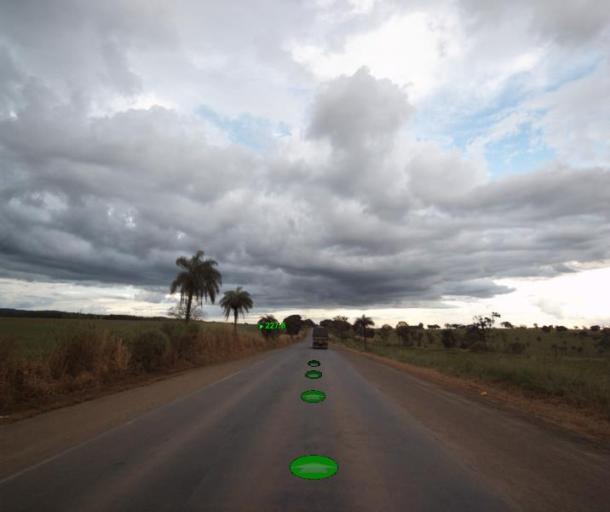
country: BR
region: Goias
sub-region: Uruacu
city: Uruacu
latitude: -14.7501
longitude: -49.2529
